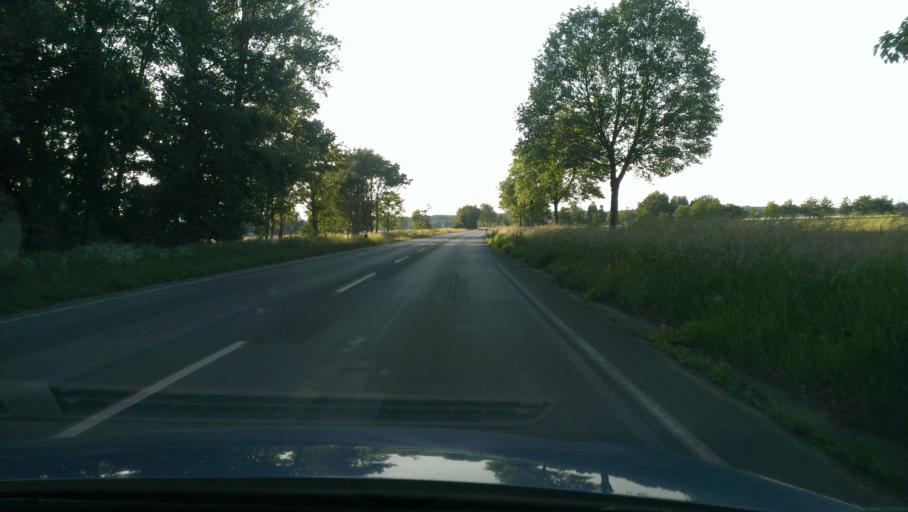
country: DE
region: North Rhine-Westphalia
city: Sendenhorst
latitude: 51.8479
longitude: 7.7997
